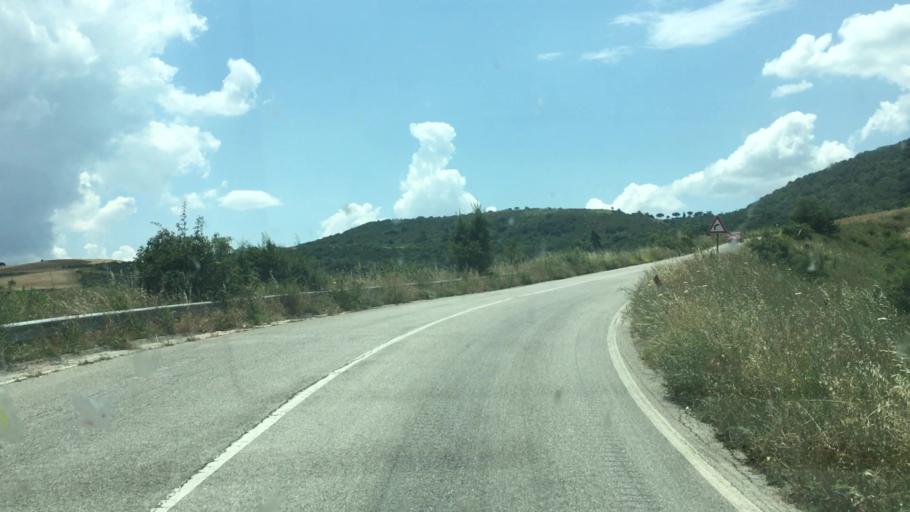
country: IT
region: Basilicate
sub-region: Provincia di Potenza
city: Tolve
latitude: 40.6912
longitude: 15.9873
